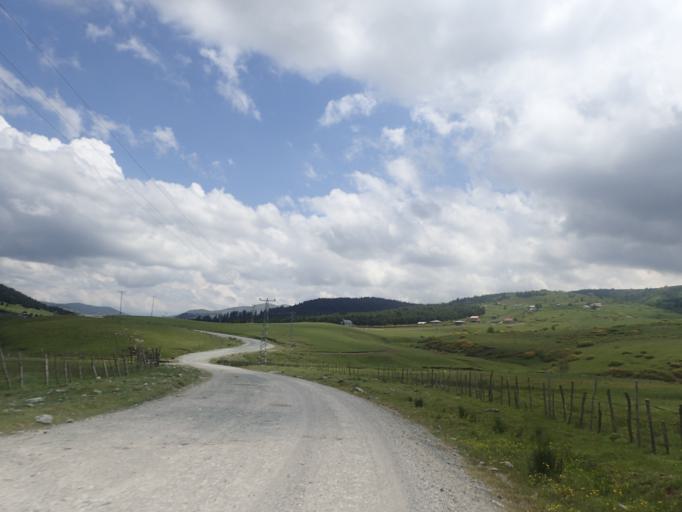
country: TR
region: Ordu
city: Topcam
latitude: 40.6848
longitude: 37.9308
